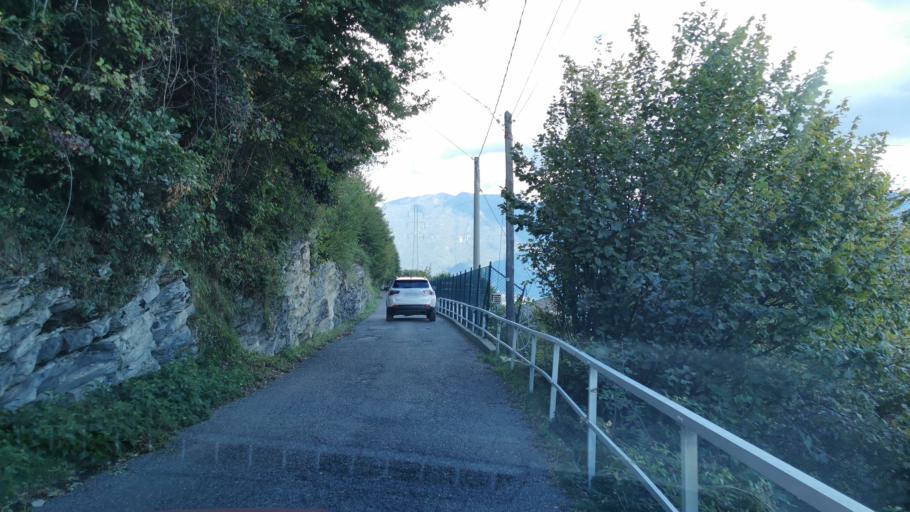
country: IT
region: Lombardy
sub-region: Provincia di Como
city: Cernobbio
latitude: 45.8556
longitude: 9.0772
